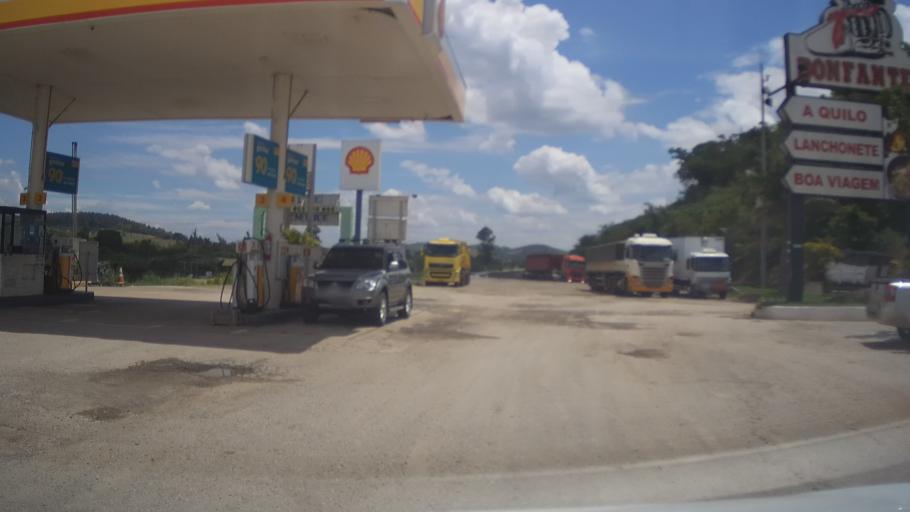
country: BR
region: Minas Gerais
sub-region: Tres Coracoes
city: Tres Coracoes
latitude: -21.6650
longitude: -45.3090
